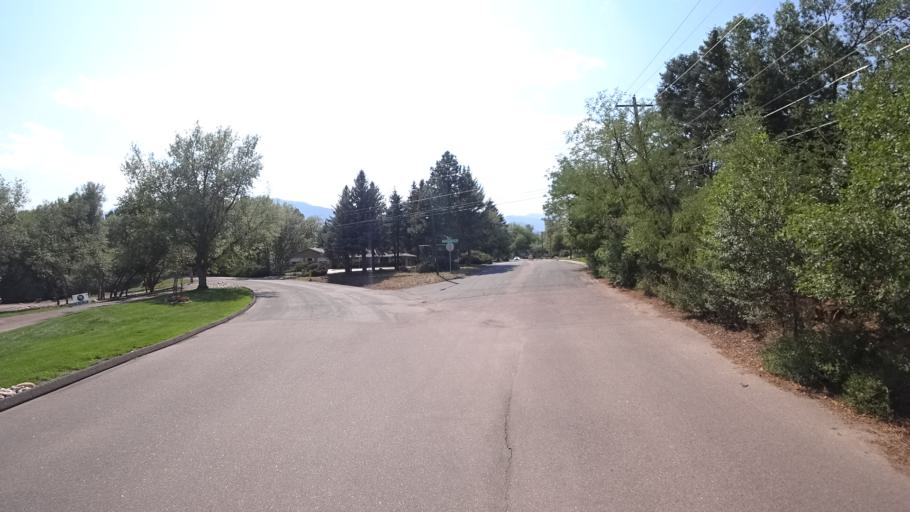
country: US
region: Colorado
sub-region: El Paso County
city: Colorado Springs
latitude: 38.7982
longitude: -104.8333
